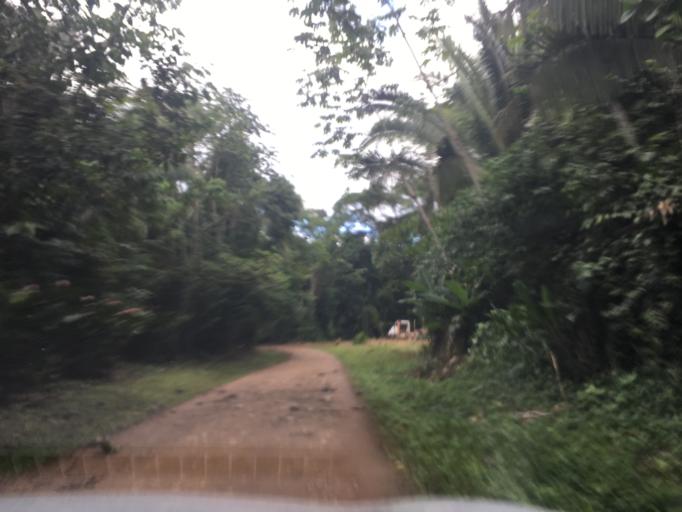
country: BZ
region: Stann Creek
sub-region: Dangriga
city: Dangriga
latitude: 16.9328
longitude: -88.3808
